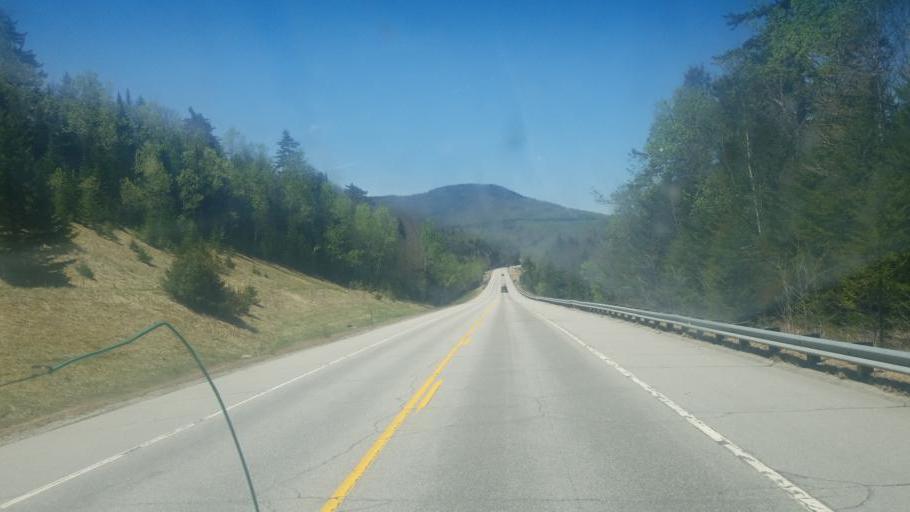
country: US
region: New Hampshire
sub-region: Grafton County
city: Deerfield
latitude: 44.2670
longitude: -71.4860
